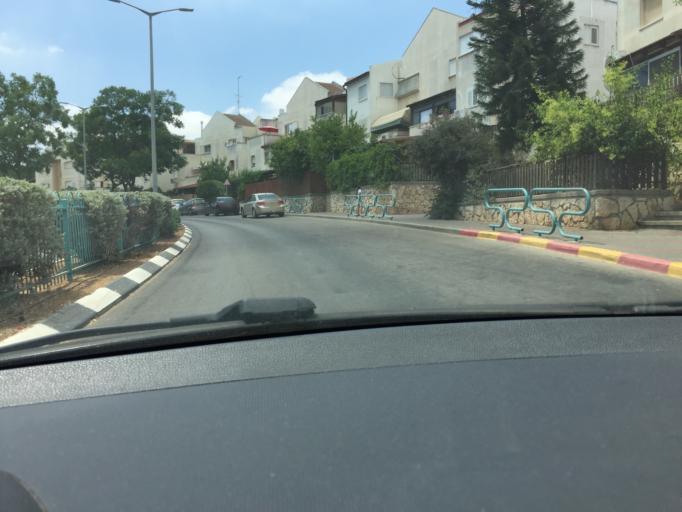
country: IL
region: Jerusalem
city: Ariel
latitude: 32.1075
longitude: 35.1892
